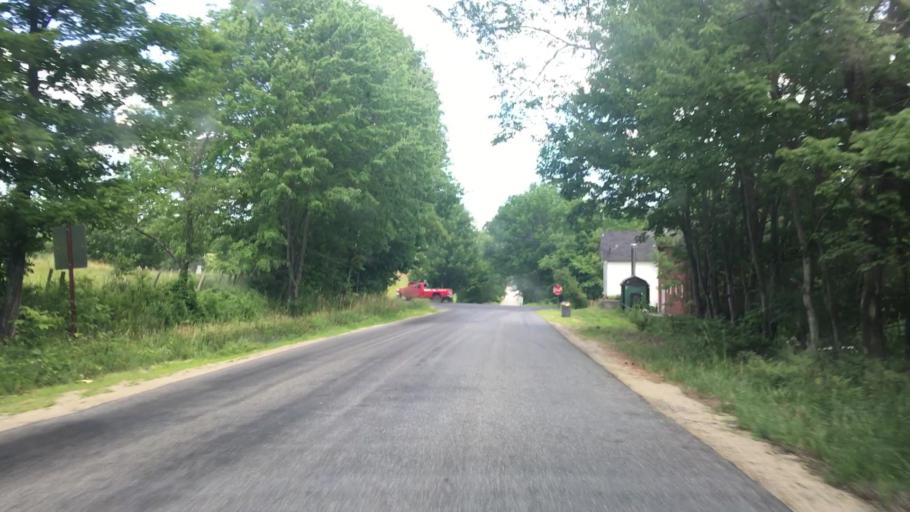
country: US
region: Maine
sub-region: Franklin County
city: Jay
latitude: 44.5375
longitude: -70.1906
